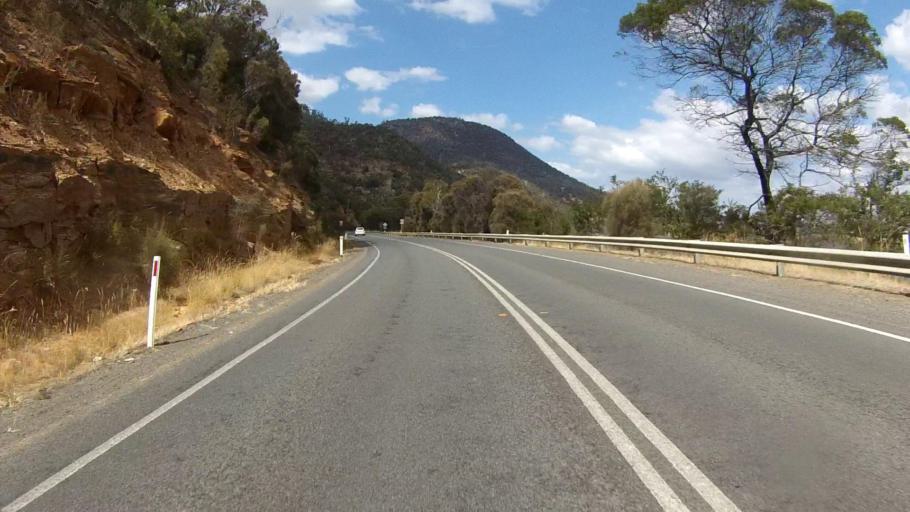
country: AU
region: Tasmania
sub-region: Brighton
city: Old Beach
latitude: -42.7841
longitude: 147.2879
